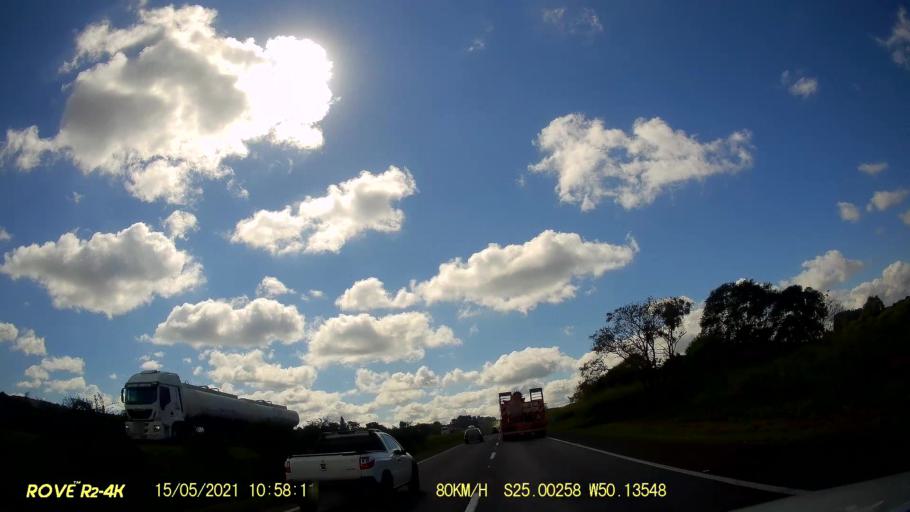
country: BR
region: Parana
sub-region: Carambei
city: Carambei
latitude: -25.0027
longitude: -50.1360
